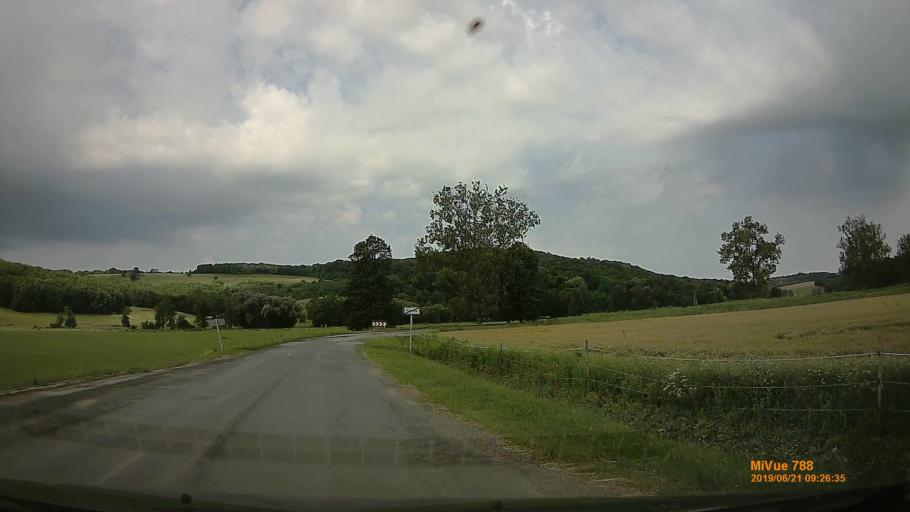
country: HU
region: Somogy
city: Taszar
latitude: 46.2736
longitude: 17.9044
